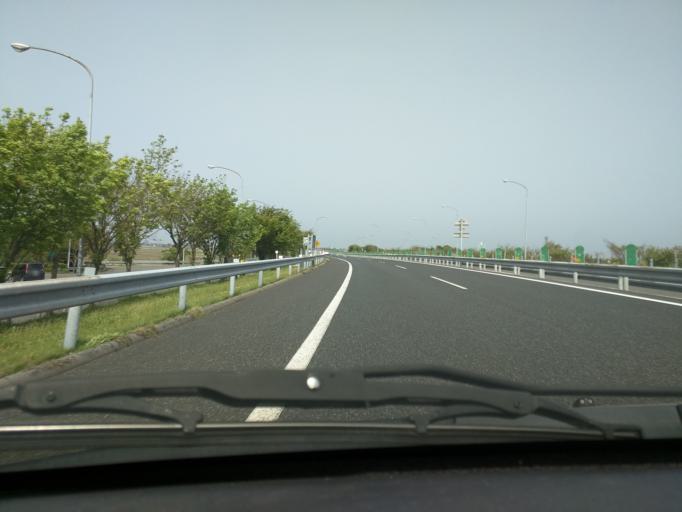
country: JP
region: Niigata
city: Kameda-honcho
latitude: 37.8476
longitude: 139.0616
